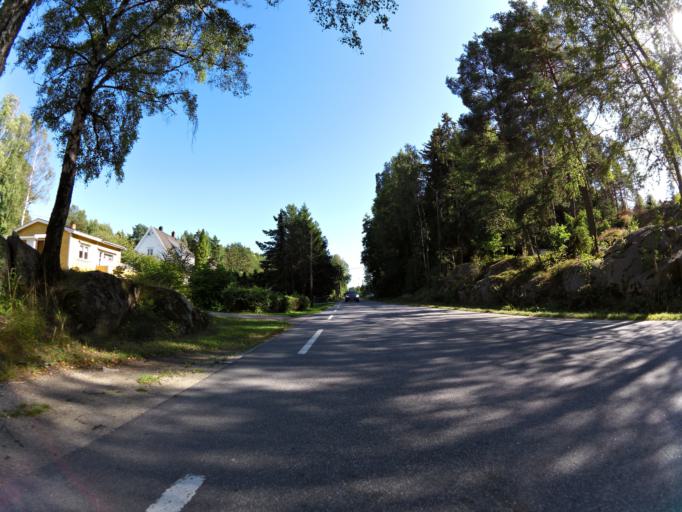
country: NO
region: Ostfold
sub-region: Fredrikstad
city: Fredrikstad
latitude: 59.1813
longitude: 10.8388
